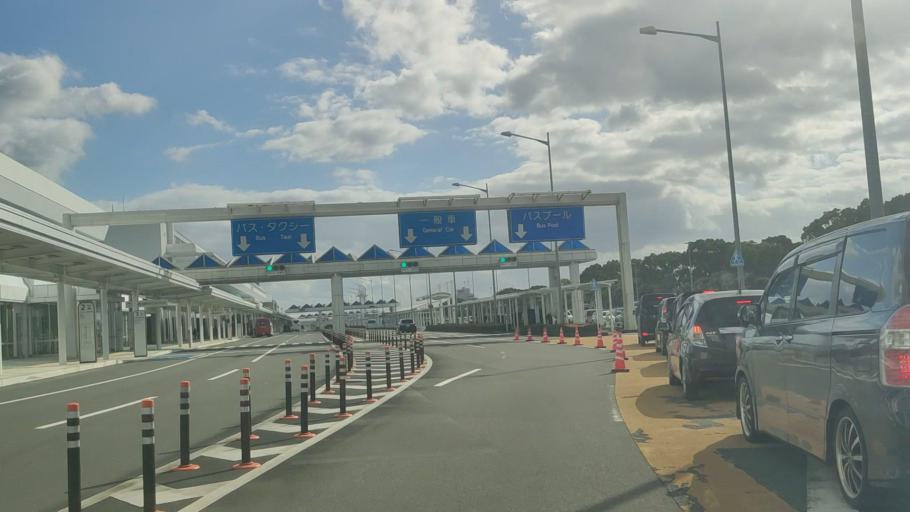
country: JP
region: Kagoshima
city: Kajiki
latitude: 31.8031
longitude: 130.7154
